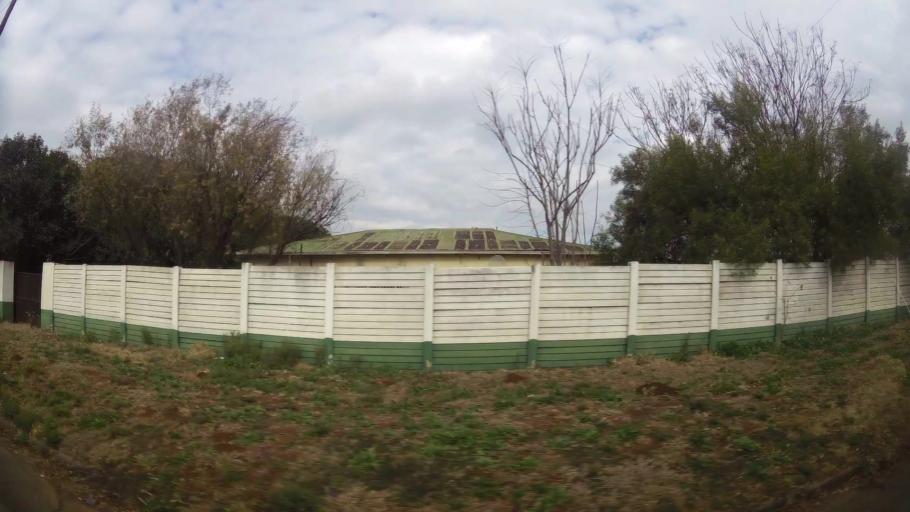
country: ZA
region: Gauteng
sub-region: Sedibeng District Municipality
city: Meyerton
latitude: -26.5980
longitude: 27.9989
